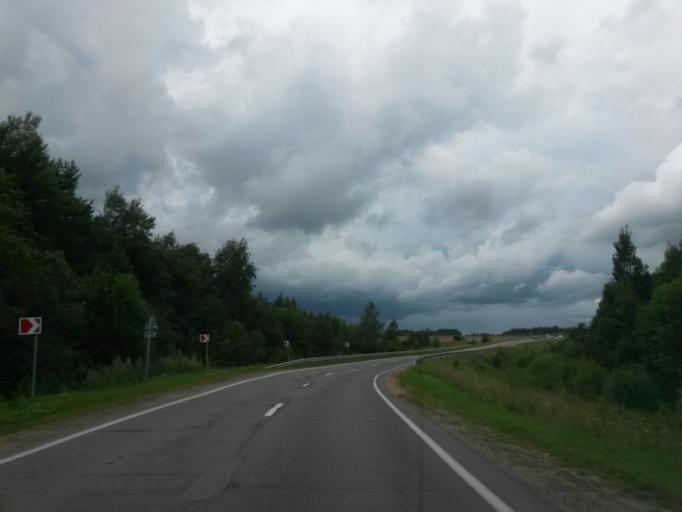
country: RU
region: Jaroslavl
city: Konstantinovskiy
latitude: 57.8586
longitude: 39.6159
